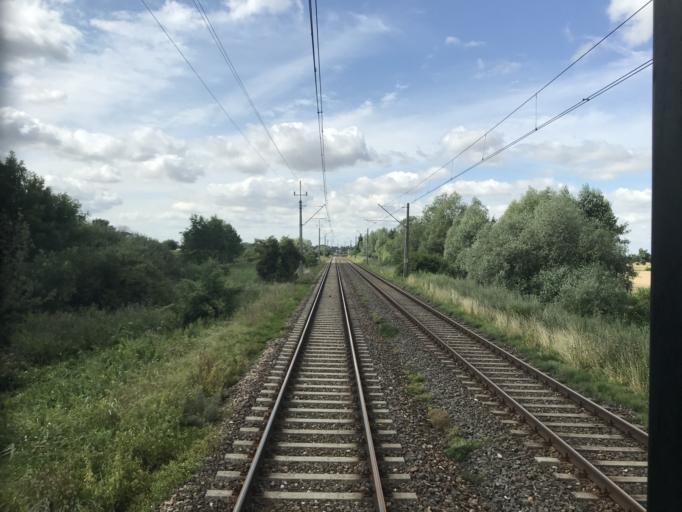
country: PL
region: Warmian-Masurian Voivodeship
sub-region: Powiat elblaski
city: Gronowo Elblaskie
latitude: 54.0988
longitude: 19.3250
